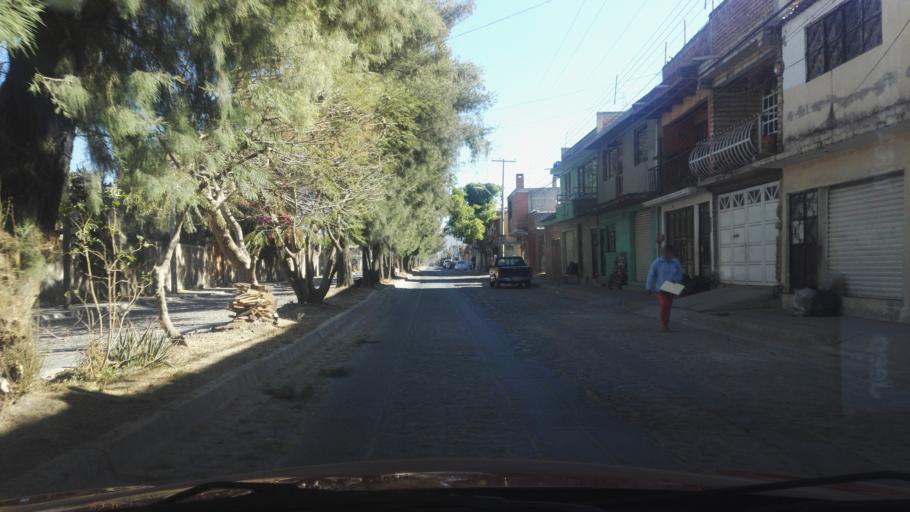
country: MX
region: Guanajuato
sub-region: Leon
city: Fraccionamiento Paraiso Real
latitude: 21.0936
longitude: -101.6067
